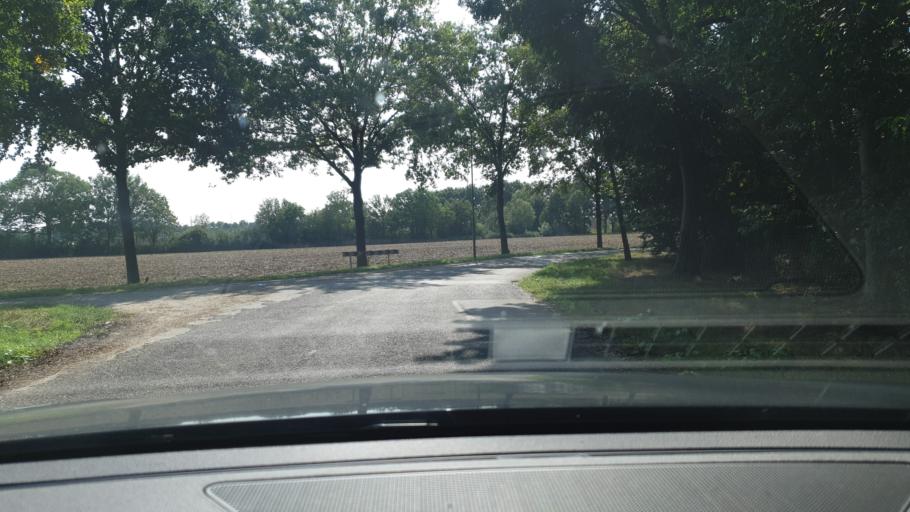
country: NL
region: Limburg
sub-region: Gemeente Sittard-Geleen
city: Born
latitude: 51.0543
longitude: 5.8253
